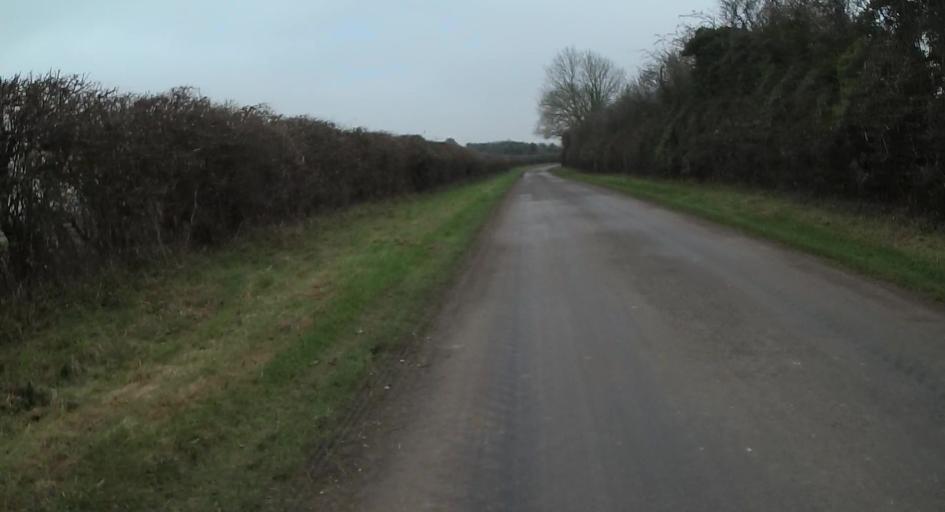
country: GB
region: England
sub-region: Hampshire
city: Kings Worthy
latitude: 51.1120
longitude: -1.2111
